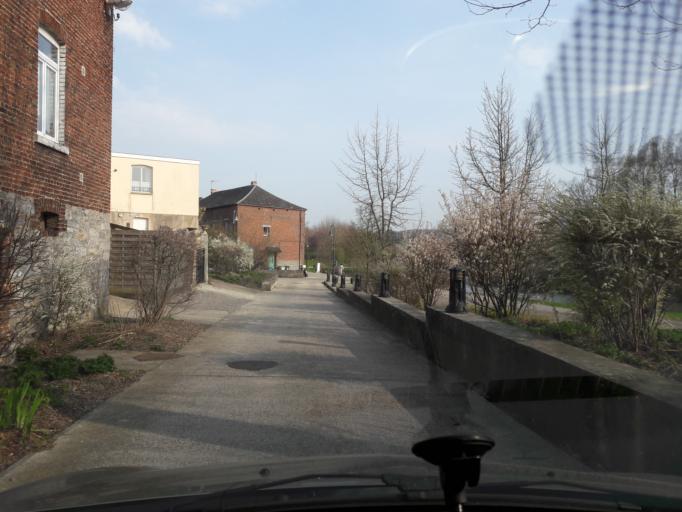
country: FR
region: Nord-Pas-de-Calais
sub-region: Departement du Nord
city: Boussois
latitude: 50.2890
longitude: 4.0437
